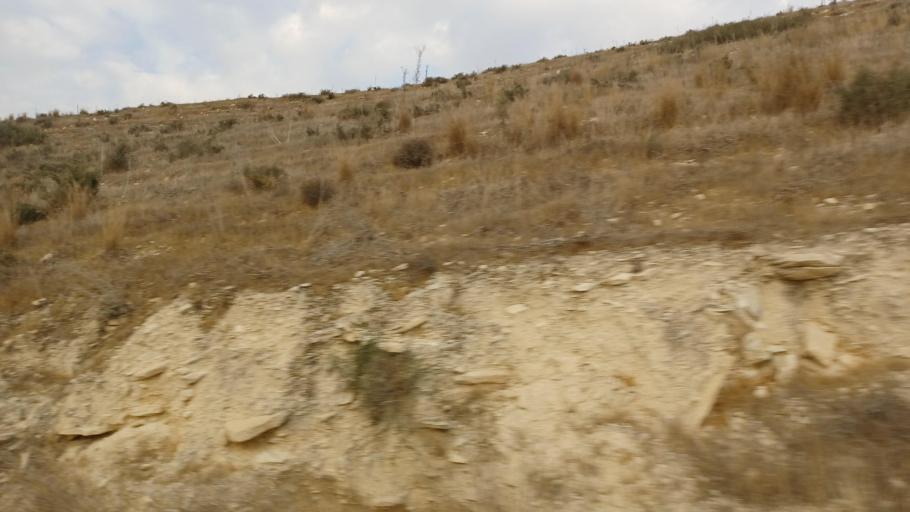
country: CY
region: Larnaka
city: Troulloi
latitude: 35.0265
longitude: 33.5739
